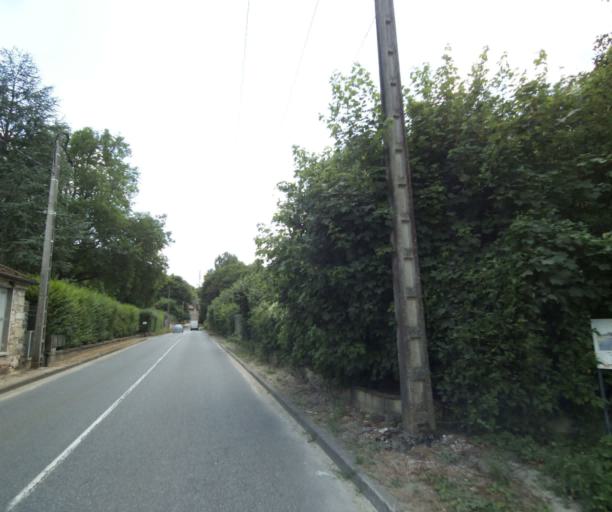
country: FR
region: Ile-de-France
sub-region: Departement de Seine-et-Marne
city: Hericy
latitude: 48.4627
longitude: 2.7729
